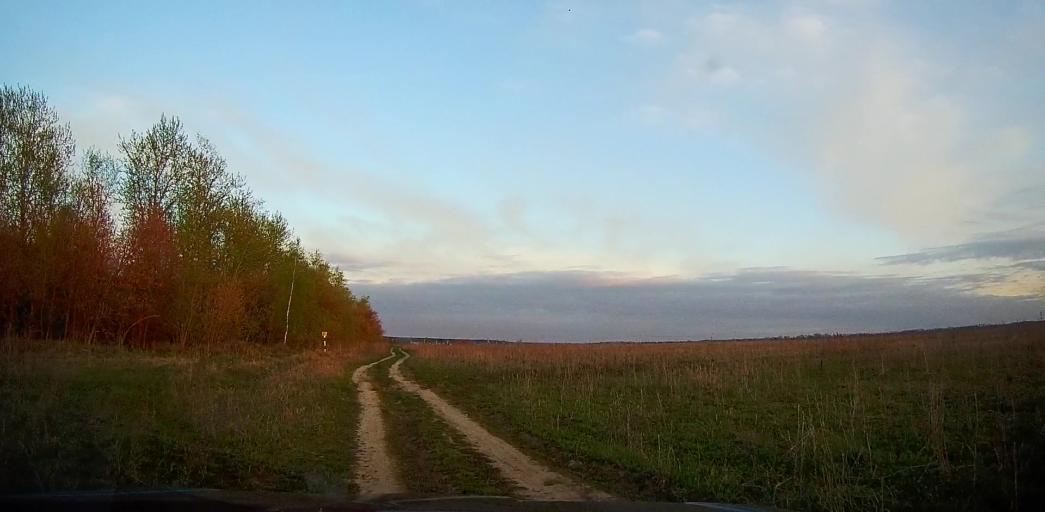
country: RU
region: Moskovskaya
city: Peski
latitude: 55.2338
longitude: 38.7290
